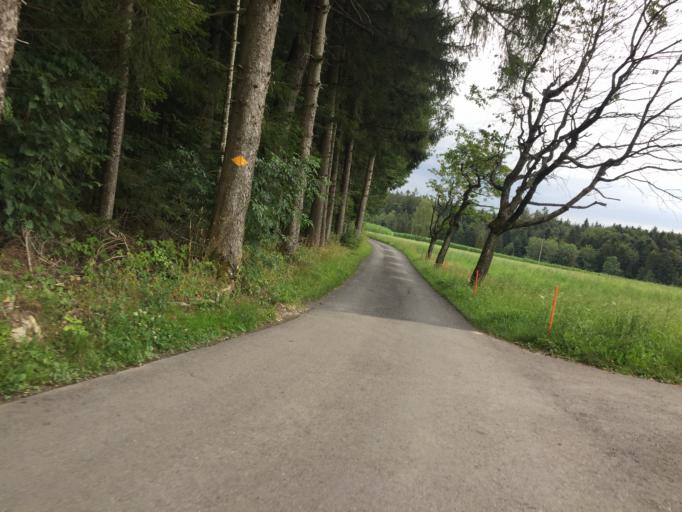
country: CH
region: Bern
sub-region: Bern-Mittelland District
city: Stettlen
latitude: 46.9438
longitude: 7.5232
